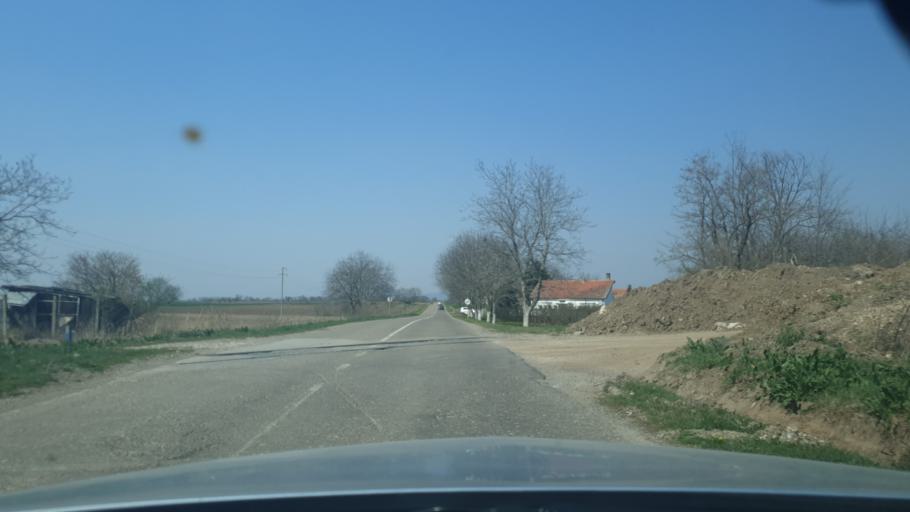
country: RS
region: Autonomna Pokrajina Vojvodina
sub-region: Sremski Okrug
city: Ruma
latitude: 45.0115
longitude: 19.7830
